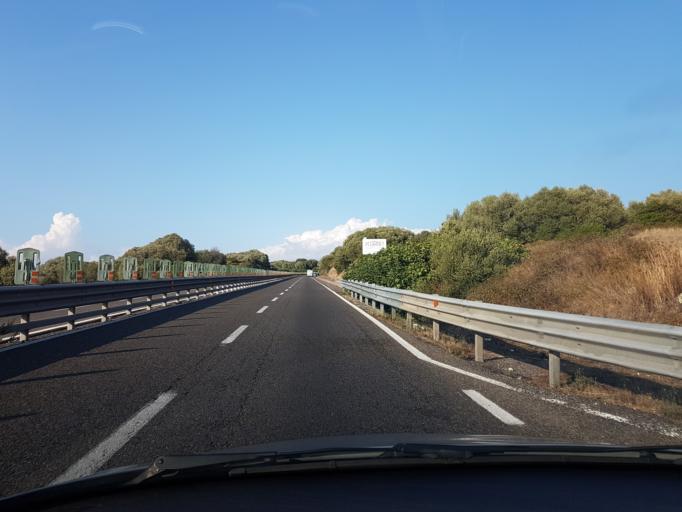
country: IT
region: Sardinia
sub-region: Provincia di Oristano
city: Paulilatino
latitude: 40.0565
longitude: 8.7167
